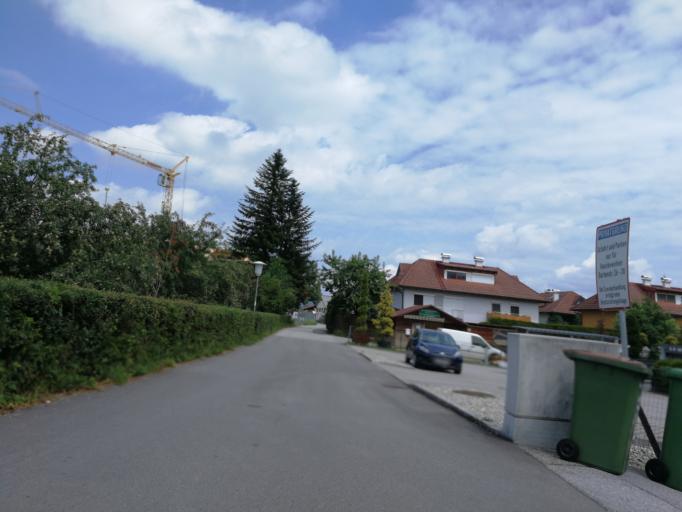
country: DE
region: Bavaria
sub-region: Upper Bavaria
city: Freilassing
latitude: 47.8065
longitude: 12.9841
